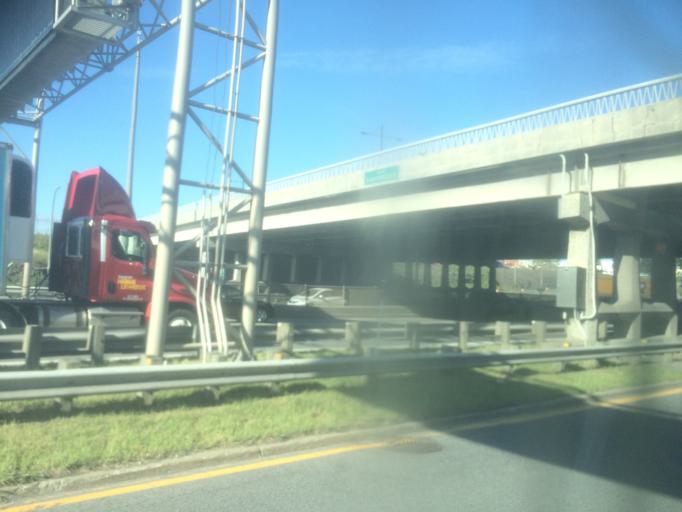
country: CA
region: Quebec
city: Montreal-Est
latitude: 45.5934
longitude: -73.5364
